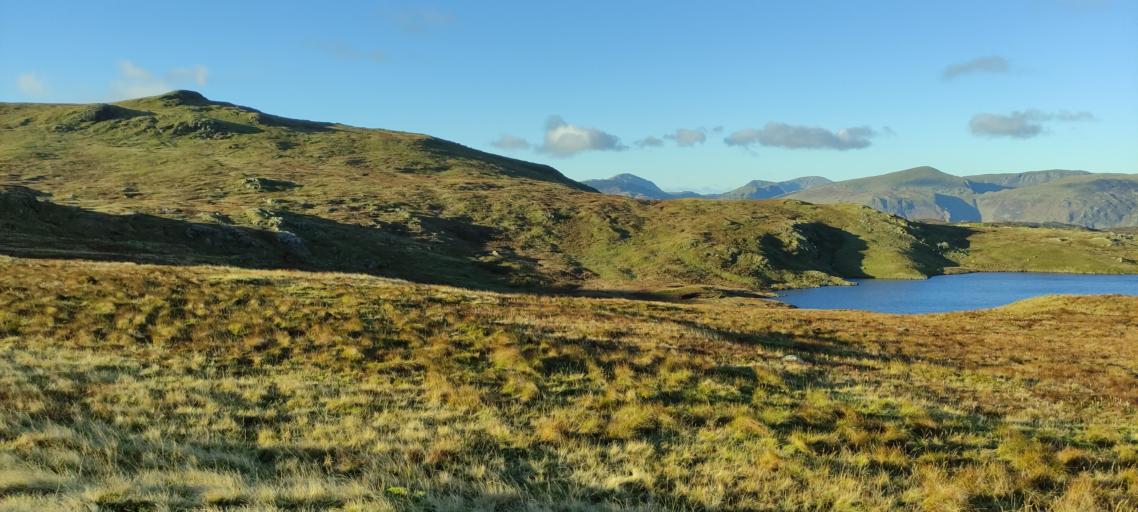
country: GB
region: England
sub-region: Cumbria
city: Keswick
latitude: 54.5157
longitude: -3.0881
